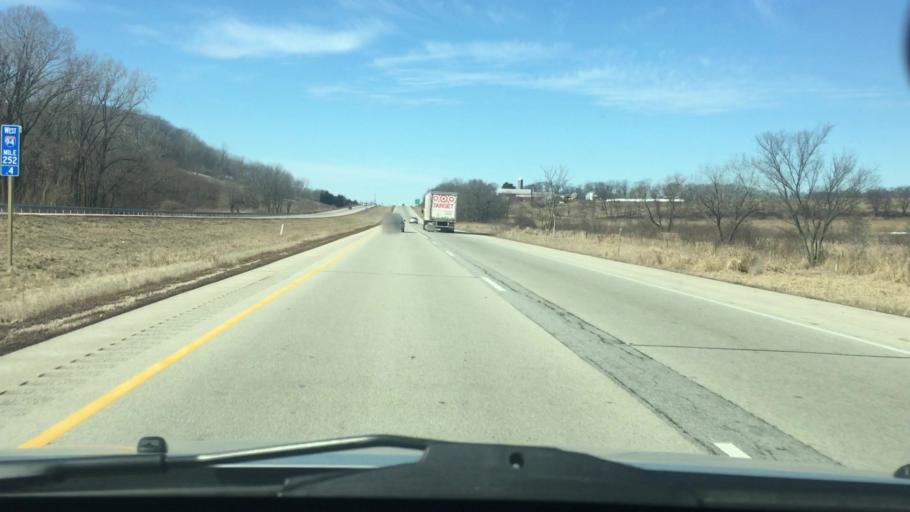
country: US
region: Wisconsin
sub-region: Dane County
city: Marshall
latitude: 43.1101
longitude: -89.0449
